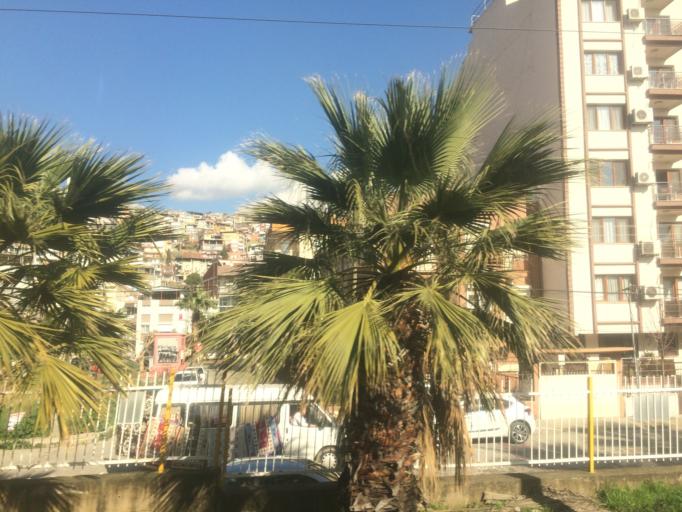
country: TR
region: Izmir
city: Karsiyaka
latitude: 38.4681
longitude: 27.1592
